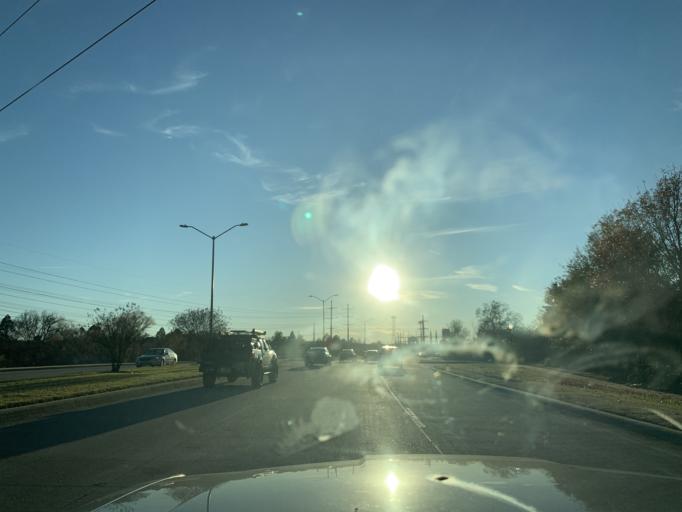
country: US
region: Texas
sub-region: Tarrant County
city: Euless
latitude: 32.8675
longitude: -97.0959
